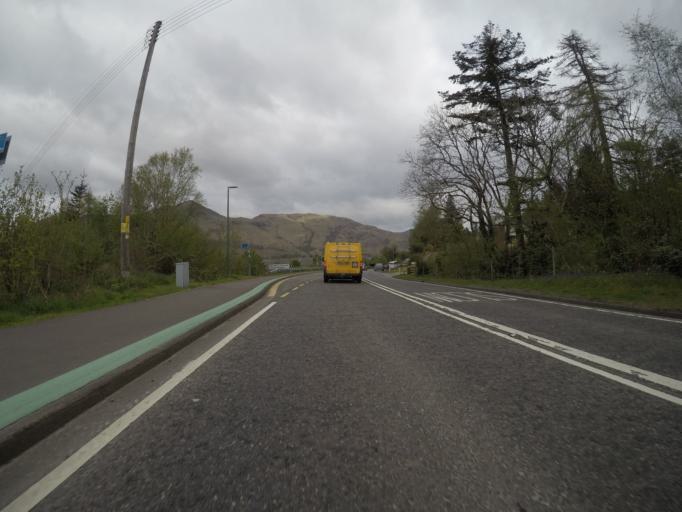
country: GB
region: Scotland
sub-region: Highland
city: Fort William
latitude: 56.7208
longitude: -5.2319
